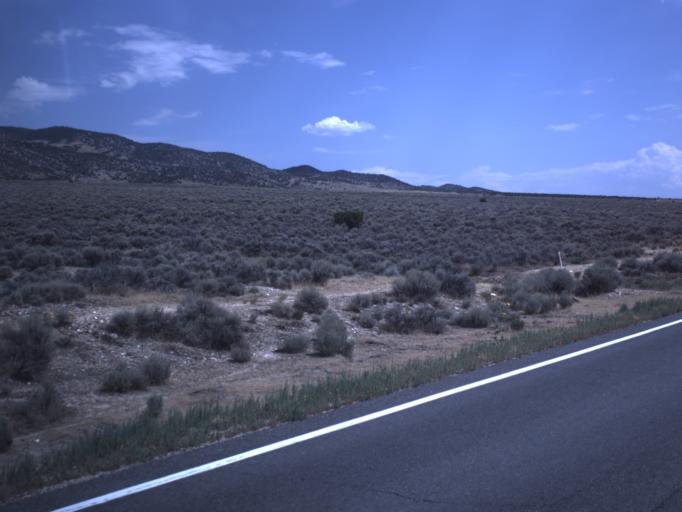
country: US
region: Utah
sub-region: Utah County
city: Eagle Mountain
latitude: 40.2791
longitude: -112.2557
